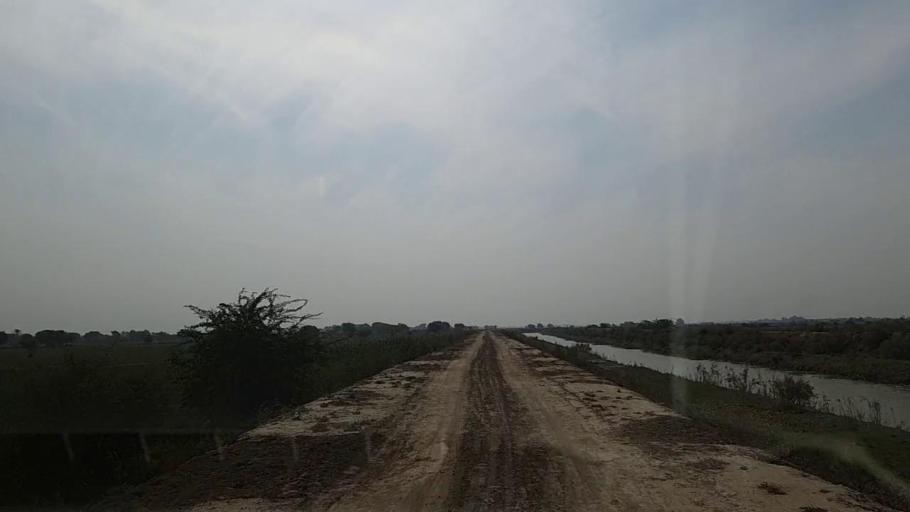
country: PK
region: Sindh
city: Mirpur Batoro
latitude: 24.6660
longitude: 68.2503
